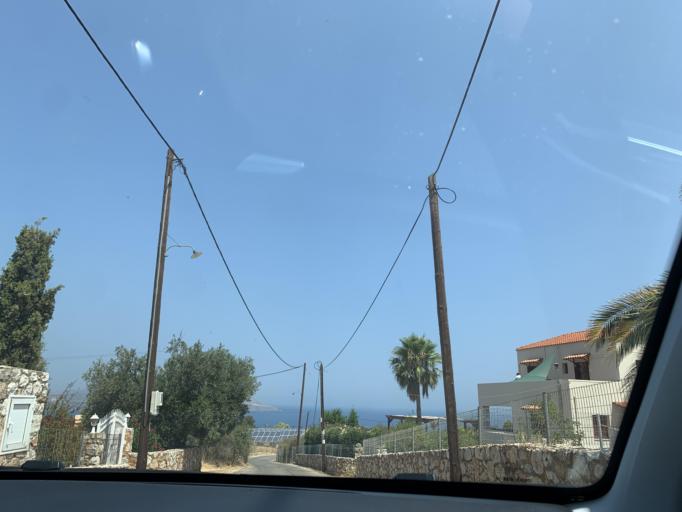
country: GR
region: Crete
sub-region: Nomos Chanias
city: Kalivai
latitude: 35.4500
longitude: 24.2276
